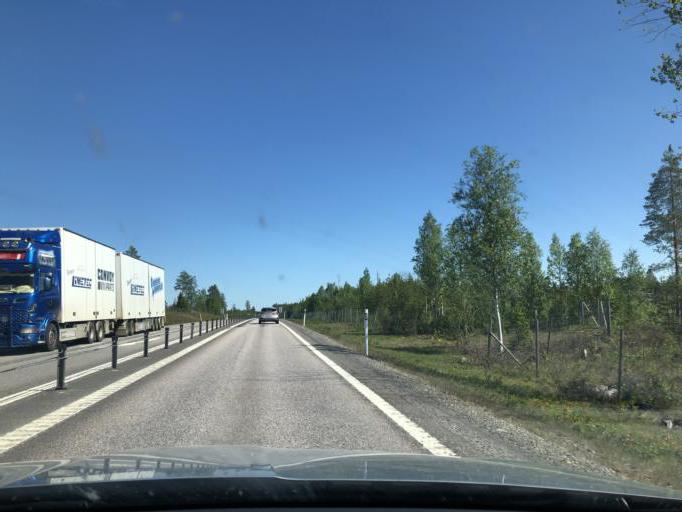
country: SE
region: Norrbotten
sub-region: Kalix Kommun
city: Toere
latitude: 65.8864
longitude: 22.5753
